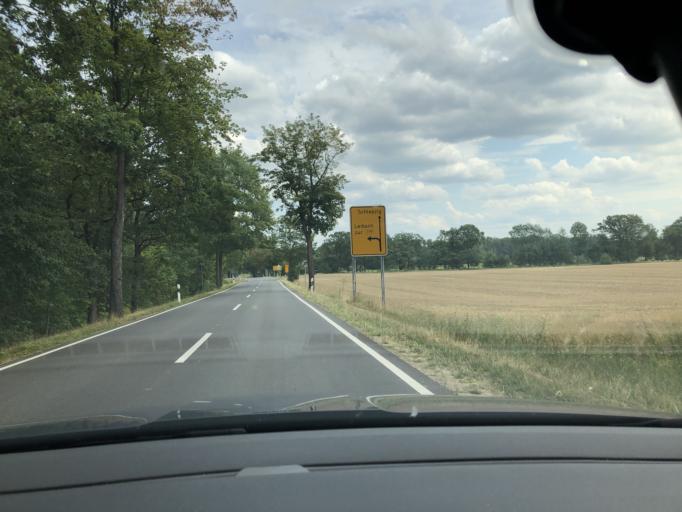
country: DE
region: Brandenburg
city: Schlepzig
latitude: 52.0344
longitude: 13.8472
